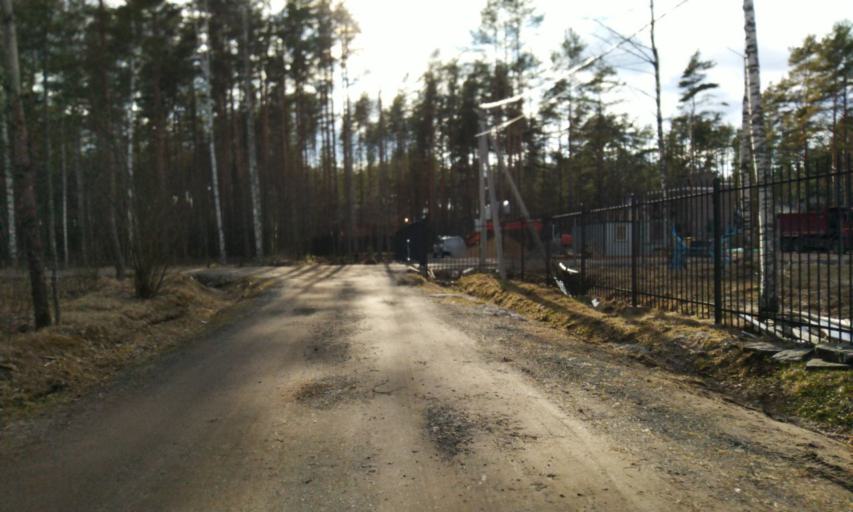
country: RU
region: Leningrad
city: Toksovo
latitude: 60.1229
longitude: 30.4758
